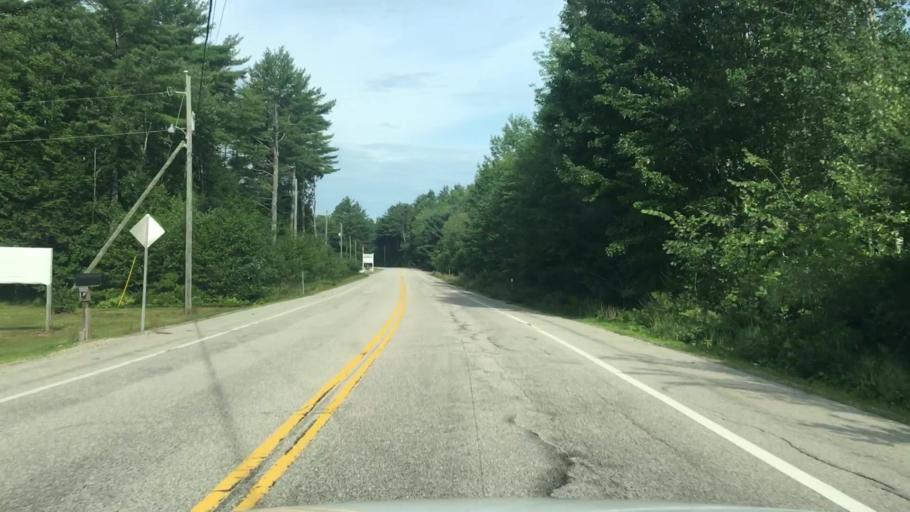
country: US
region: New Hampshire
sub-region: Carroll County
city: Effingham
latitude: 43.7971
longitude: -71.0002
